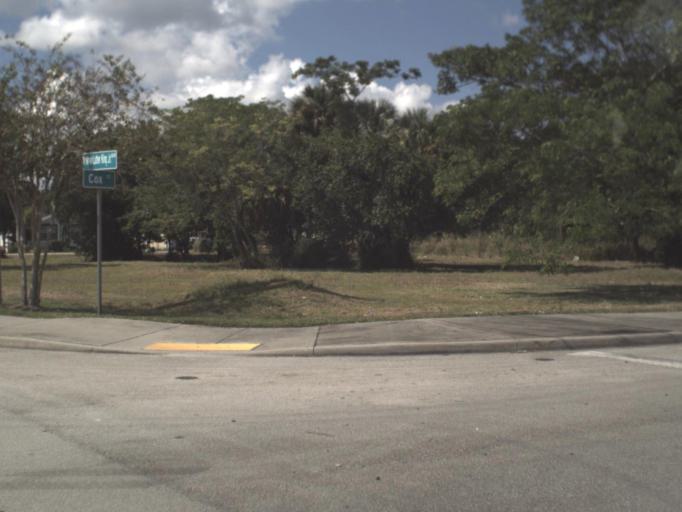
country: US
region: Florida
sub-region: Lee County
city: Fort Myers
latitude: 26.6411
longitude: -81.8490
